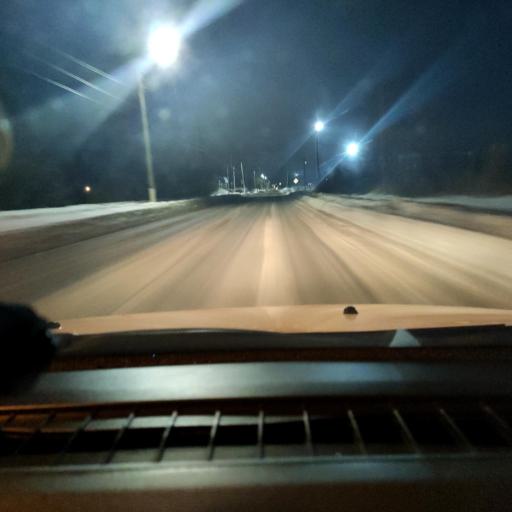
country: RU
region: Samara
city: Chapayevsk
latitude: 52.9737
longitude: 49.6976
